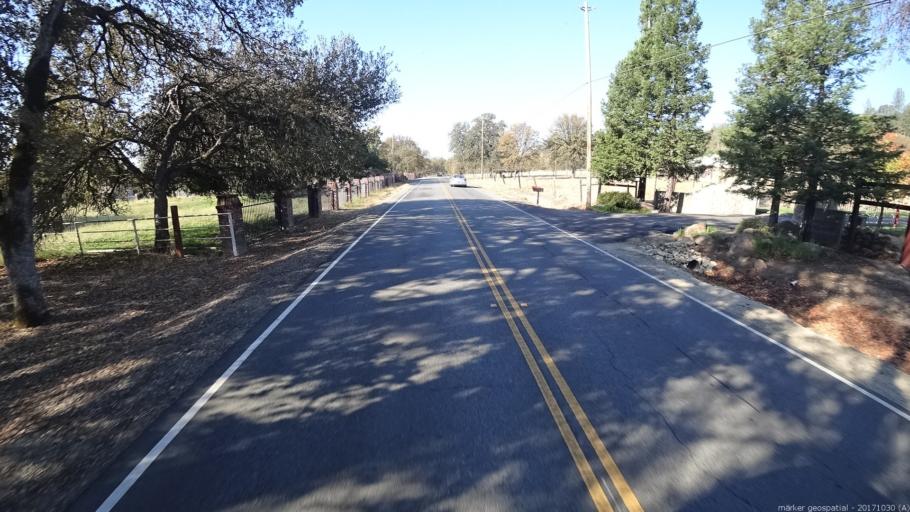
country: US
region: California
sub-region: Shasta County
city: Palo Cedro
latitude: 40.5677
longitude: -122.1988
